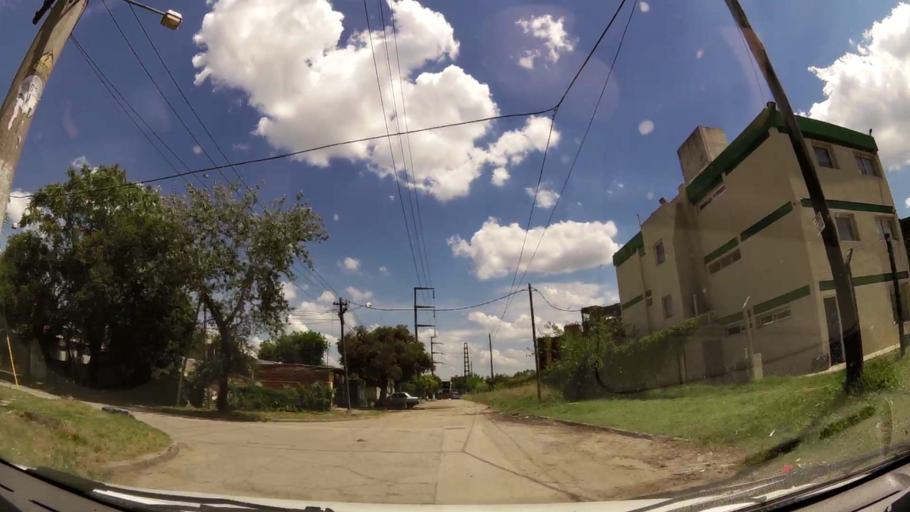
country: AR
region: Buenos Aires
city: Ituzaingo
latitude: -34.6453
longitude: -58.6880
